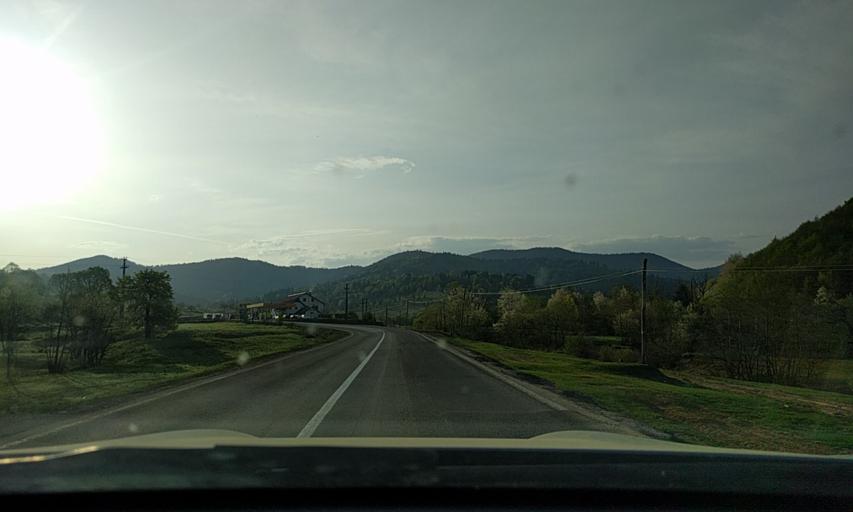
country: RO
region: Covasna
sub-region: Comuna Bretcu
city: Bretcu
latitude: 46.0459
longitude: 26.3231
